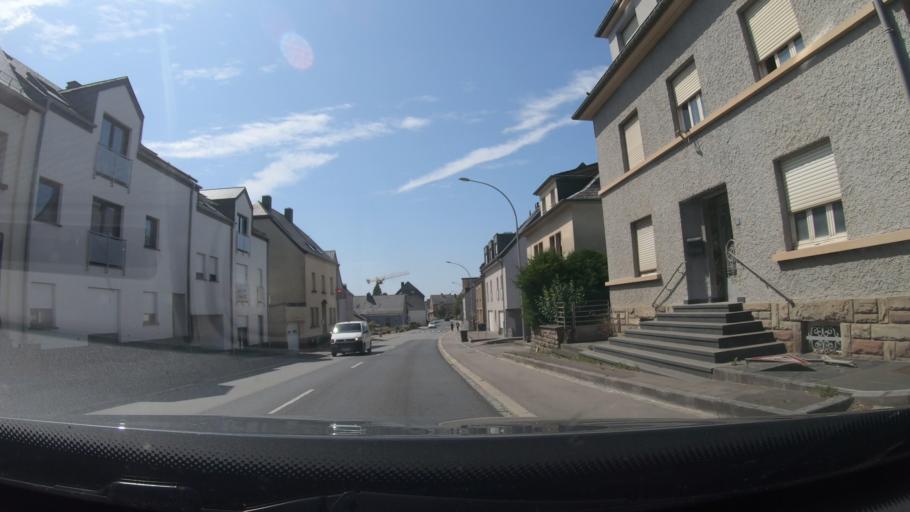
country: LU
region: Diekirch
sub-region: Canton de Clervaux
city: Hosingen
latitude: 50.0181
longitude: 6.0917
